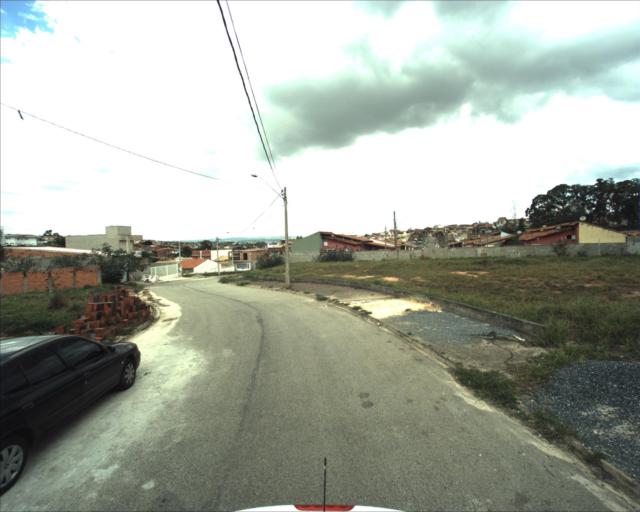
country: BR
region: Sao Paulo
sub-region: Sorocaba
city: Sorocaba
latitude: -23.4458
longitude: -47.4752
